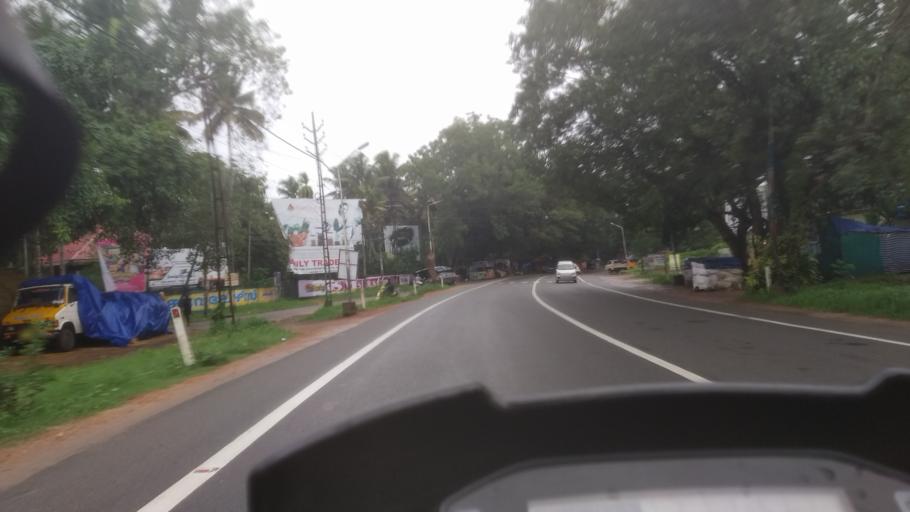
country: IN
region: Kerala
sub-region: Alappuzha
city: Kayankulam
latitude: 9.1537
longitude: 76.5106
